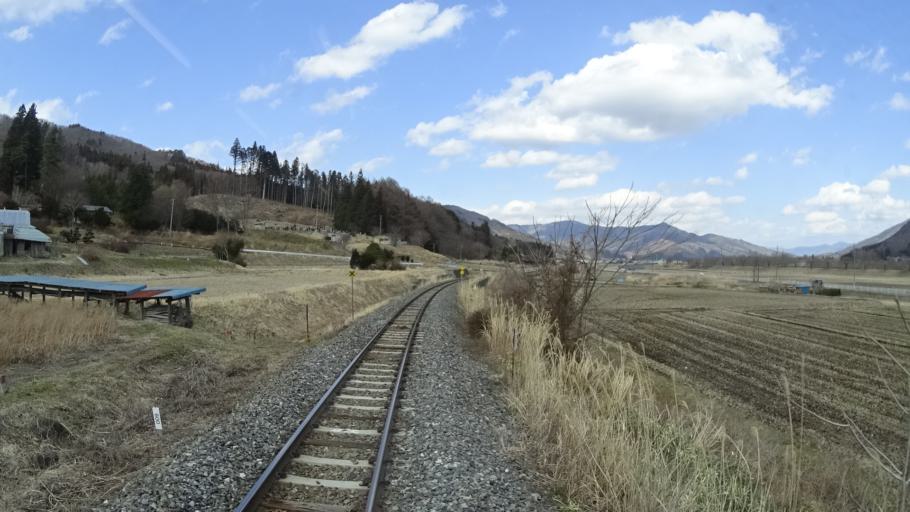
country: JP
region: Iwate
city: Tono
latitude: 39.3146
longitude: 141.4376
